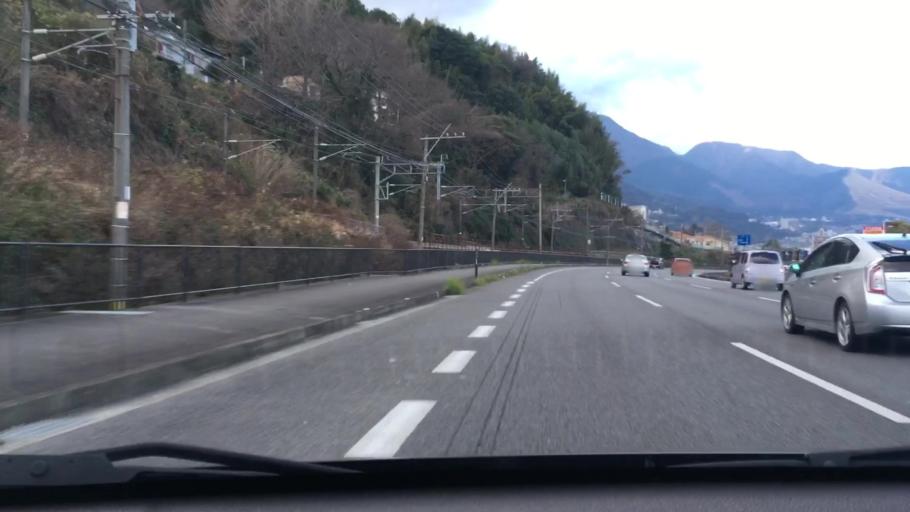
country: JP
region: Oita
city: Beppu
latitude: 33.2653
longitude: 131.5165
